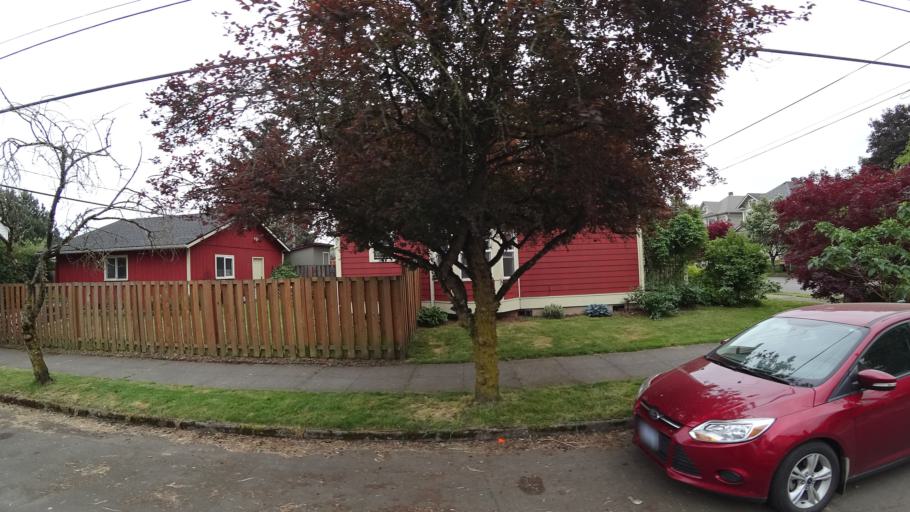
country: US
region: Oregon
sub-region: Multnomah County
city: Portland
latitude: 45.5568
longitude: -122.6699
